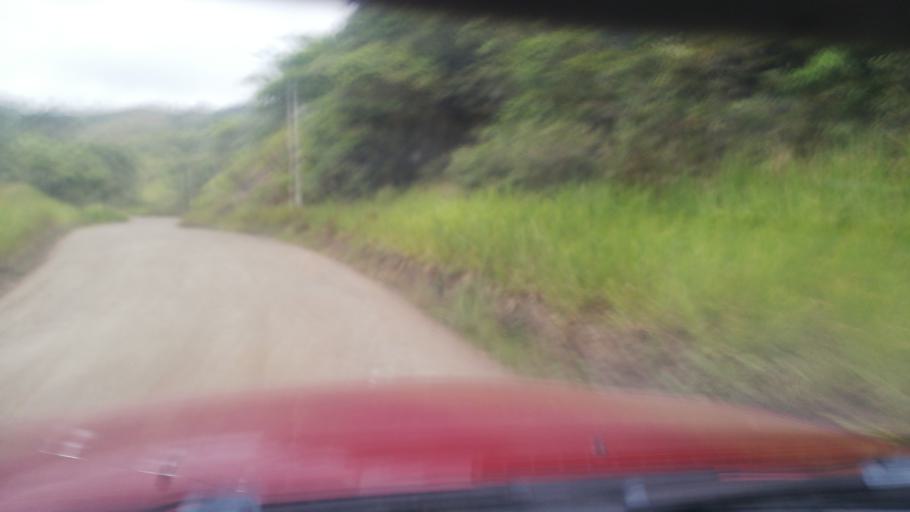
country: CO
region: Valle del Cauca
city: Cali
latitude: 3.4918
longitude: -76.5435
